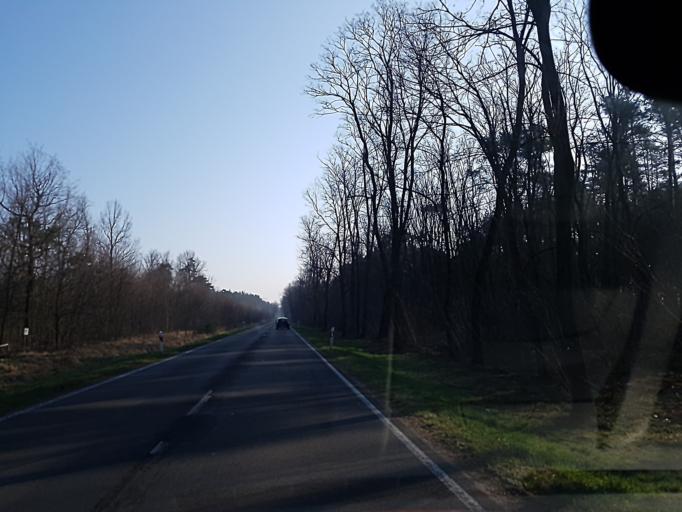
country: DE
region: Brandenburg
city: Calau
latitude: 51.7649
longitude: 14.0120
